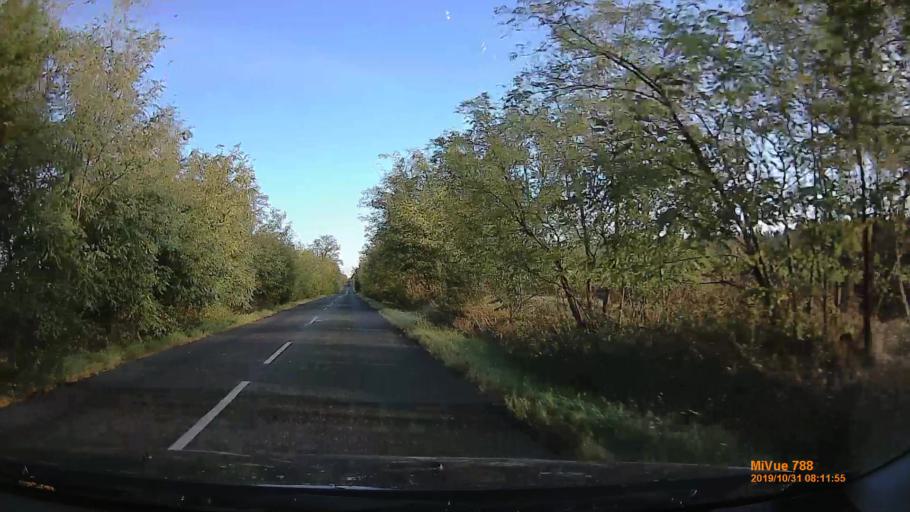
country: HU
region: Pest
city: Pilis
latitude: 47.3193
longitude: 19.5650
